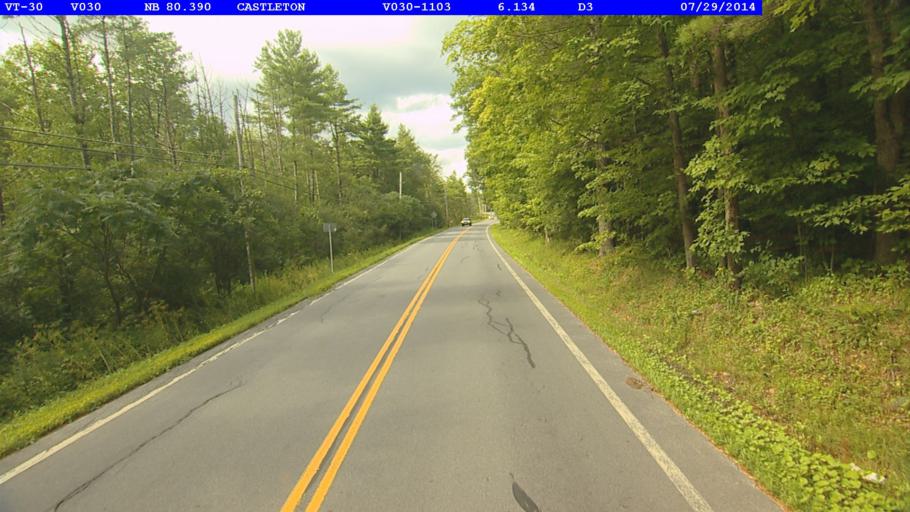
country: US
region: Vermont
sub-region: Rutland County
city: Castleton
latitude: 43.6731
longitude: -73.1917
